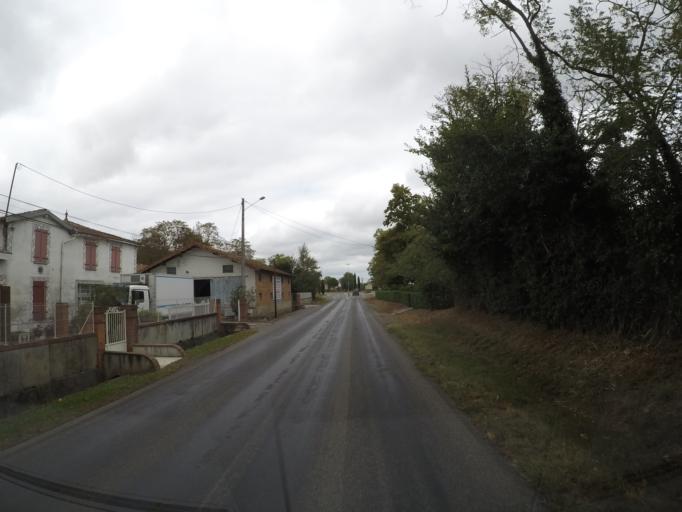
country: FR
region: Midi-Pyrenees
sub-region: Departement de l'Ariege
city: Lezat-sur-Leze
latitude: 43.2302
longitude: 1.3765
